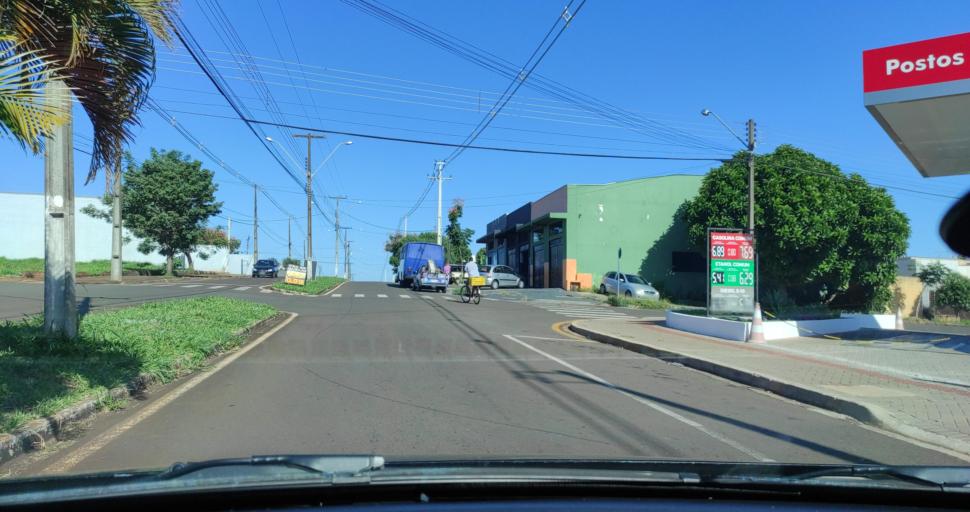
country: BR
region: Parana
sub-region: Ibipora
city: Ibipora
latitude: -23.2753
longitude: -51.0686
